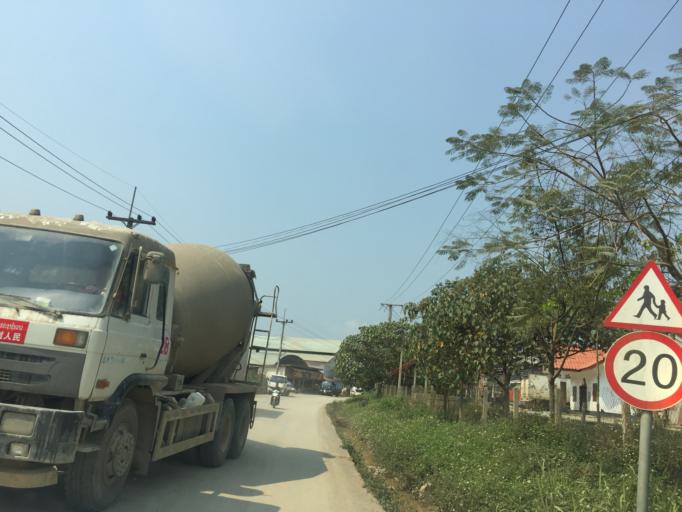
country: LA
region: Oudomxai
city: Muang Xay
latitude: 20.9062
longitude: 101.7637
